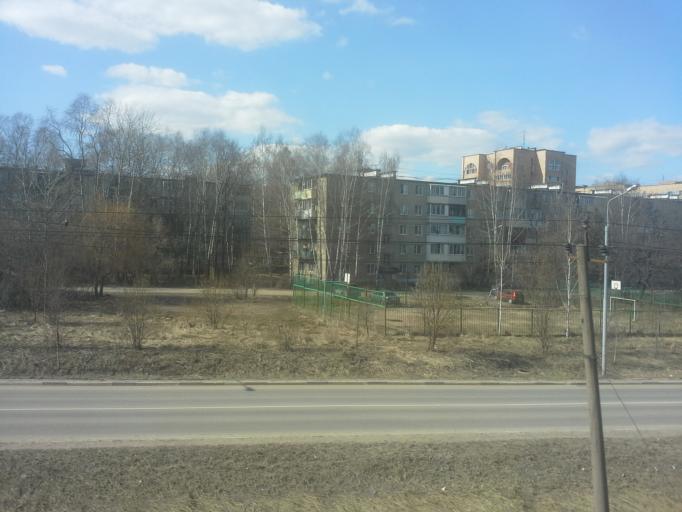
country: RU
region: Moskovskaya
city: Sergiyev Posad
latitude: 56.2950
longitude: 38.1328
